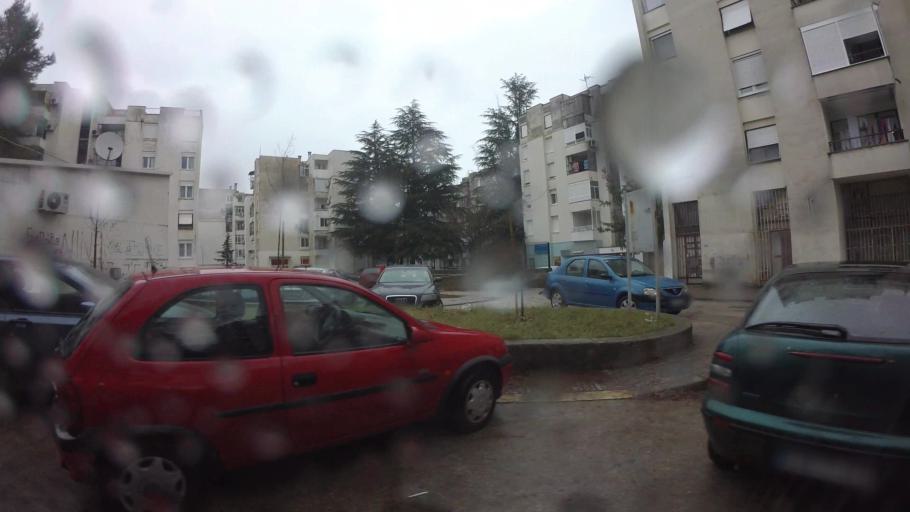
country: BA
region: Federation of Bosnia and Herzegovina
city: Cim
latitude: 43.3461
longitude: 17.7926
